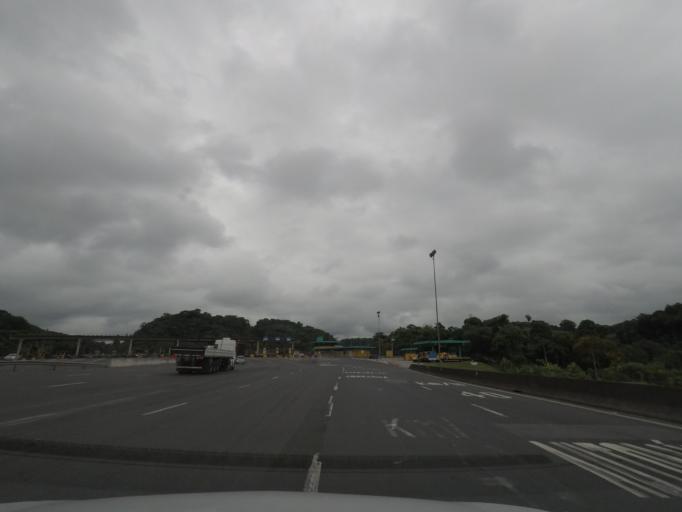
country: BR
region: Sao Paulo
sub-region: Juquia
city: Juquia
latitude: -24.3882
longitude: -47.7218
